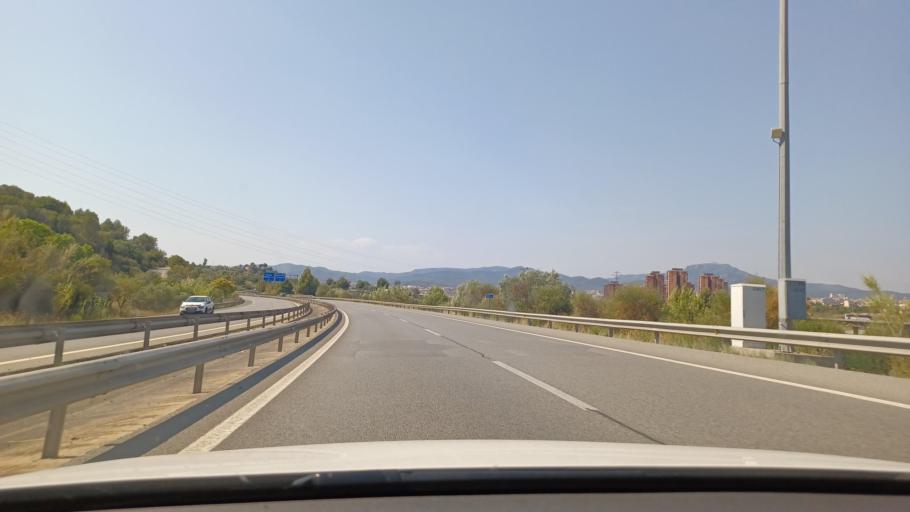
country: ES
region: Catalonia
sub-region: Provincia de Barcelona
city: Terrassa
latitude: 41.5389
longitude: 2.0192
